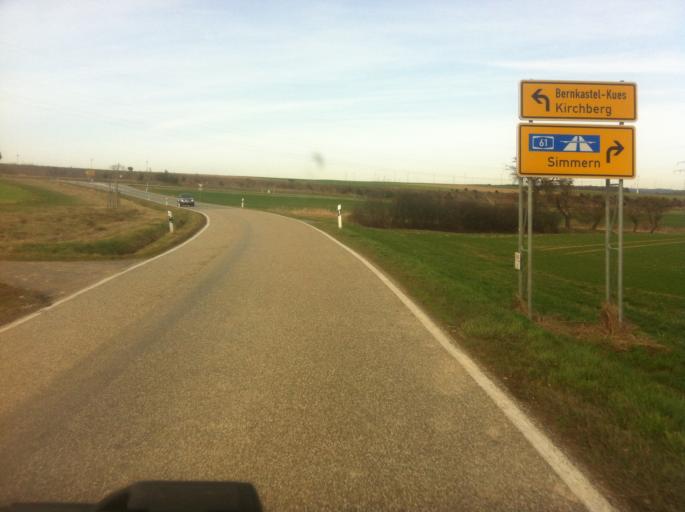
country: DE
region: Rheinland-Pfalz
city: Nannhausen
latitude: 49.9614
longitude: 7.4737
